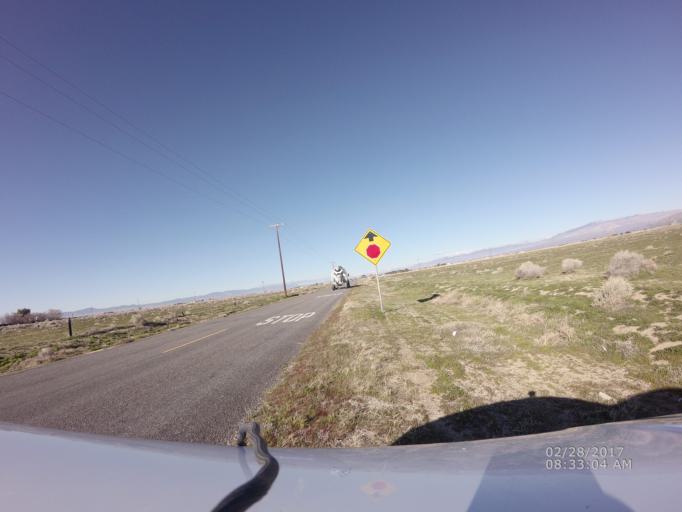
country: US
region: California
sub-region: Kern County
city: Rosamond
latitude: 34.8202
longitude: -118.2347
